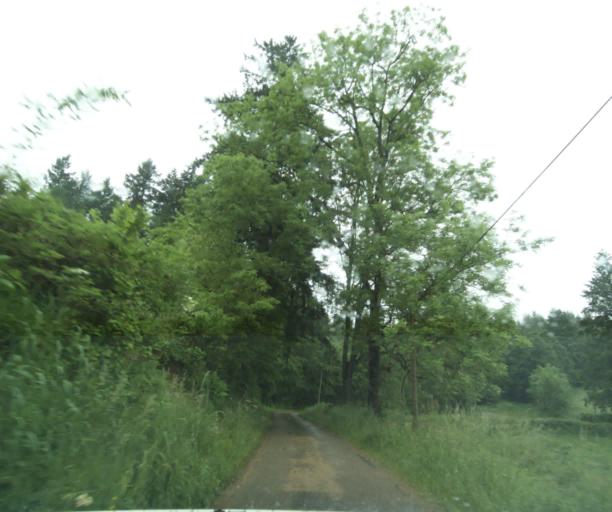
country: FR
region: Bourgogne
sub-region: Departement de Saone-et-Loire
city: La Clayette
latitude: 46.3634
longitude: 4.3643
